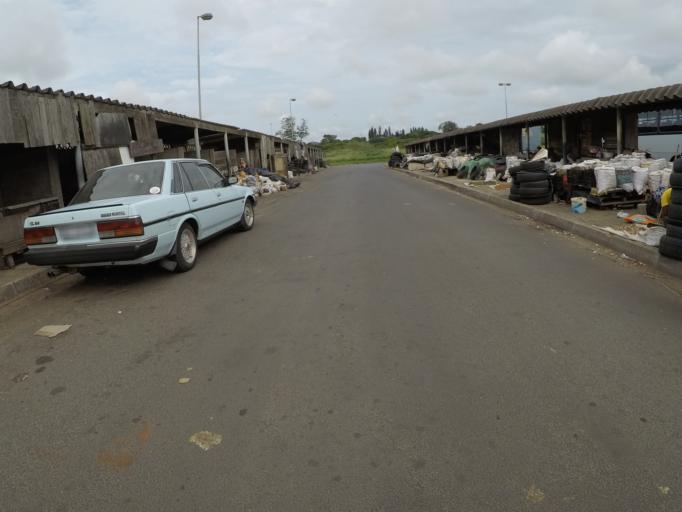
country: ZA
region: KwaZulu-Natal
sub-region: uThungulu District Municipality
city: Empangeni
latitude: -28.7741
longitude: 31.9040
